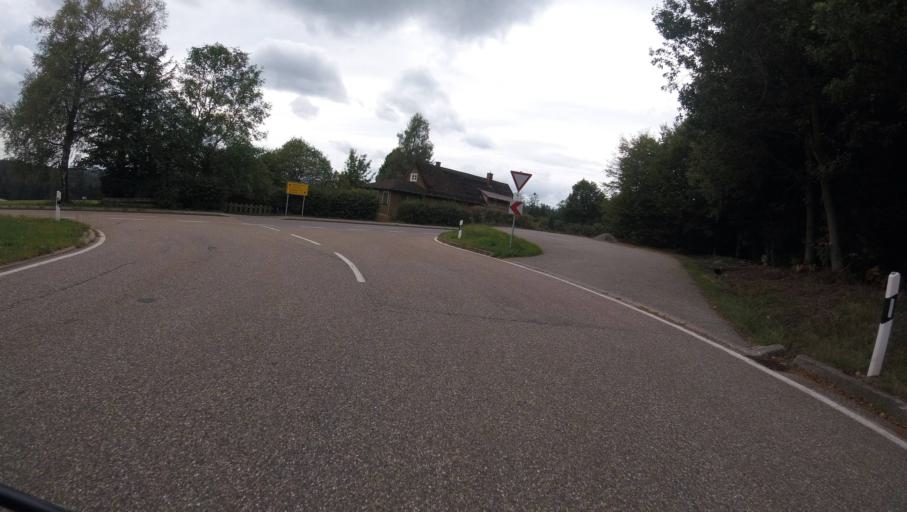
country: DE
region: Baden-Wuerttemberg
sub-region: Karlsruhe Region
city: Simmersfeld
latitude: 48.6008
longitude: 8.4444
